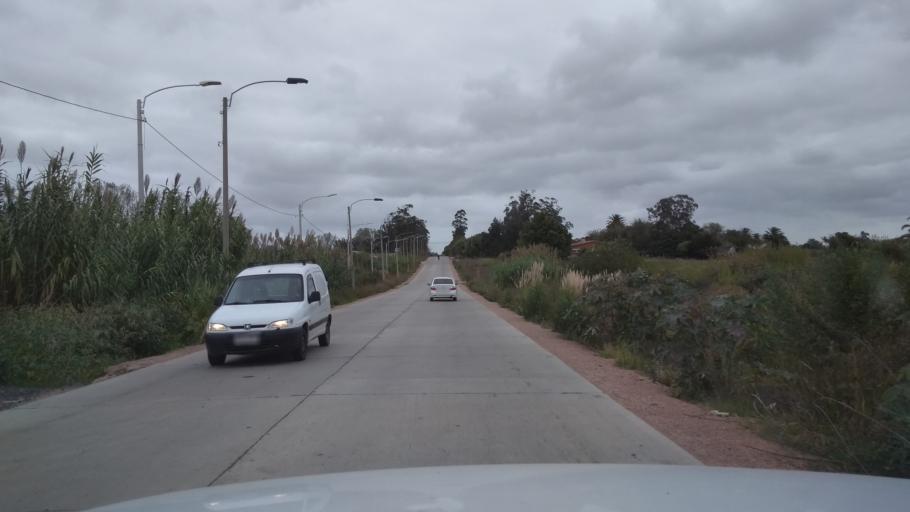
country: UY
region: Canelones
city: Toledo
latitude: -34.7919
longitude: -56.1473
